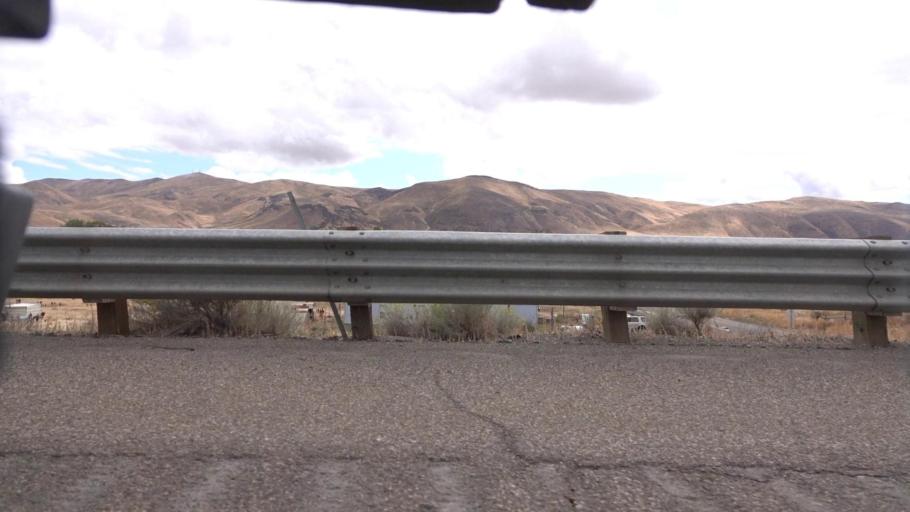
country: US
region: Nevada
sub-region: Elko County
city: Elko
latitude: 40.9062
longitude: -115.6994
